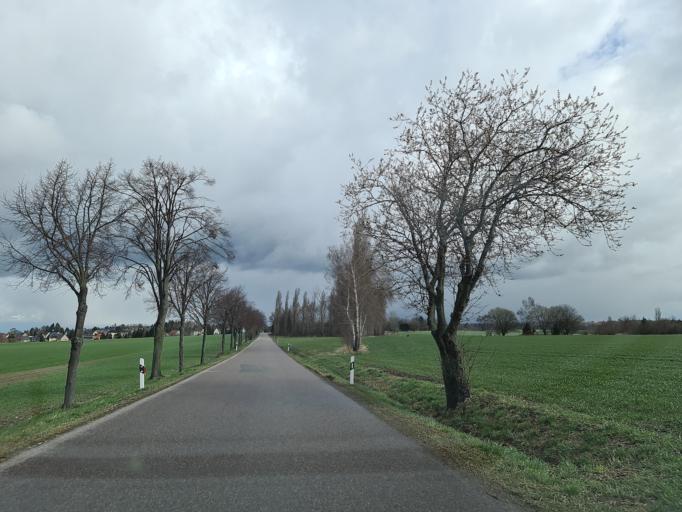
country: DE
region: Saxony
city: Limbach-Oberfrohna
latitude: 50.8414
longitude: 12.7301
